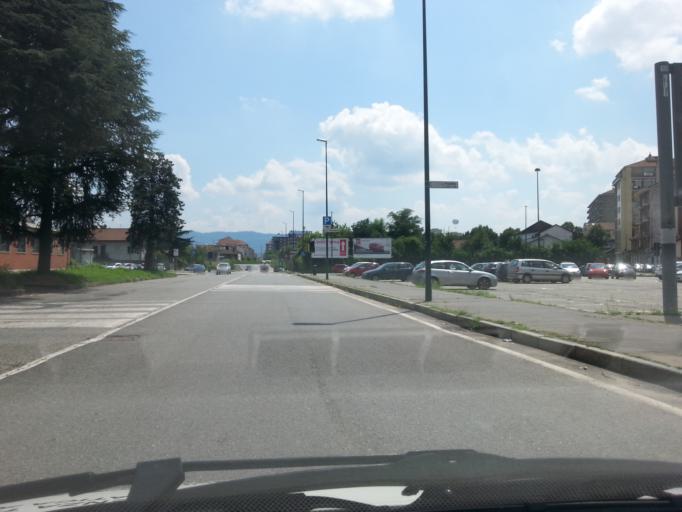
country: IT
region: Piedmont
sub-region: Provincia di Torino
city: Turin
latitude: 45.1003
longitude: 7.6848
